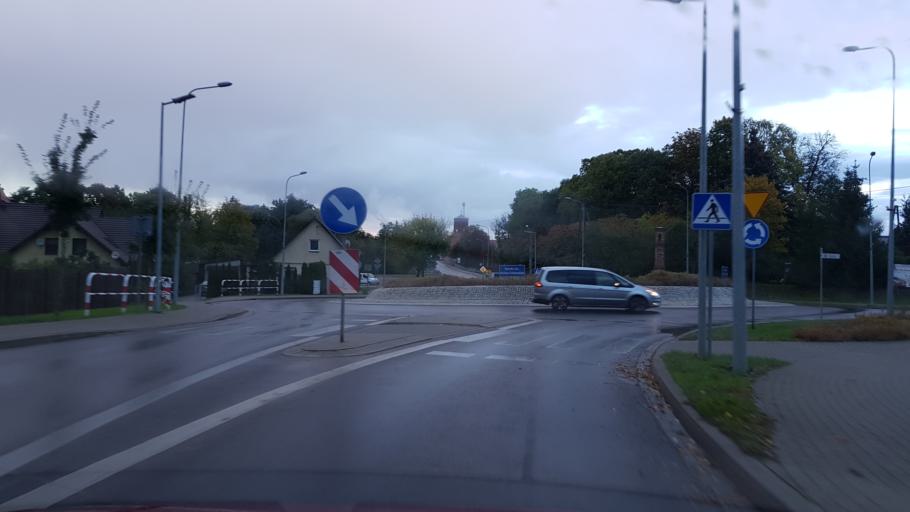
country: PL
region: Greater Poland Voivodeship
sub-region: Powiat zlotowski
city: Krajenka
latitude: 53.2971
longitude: 16.9885
